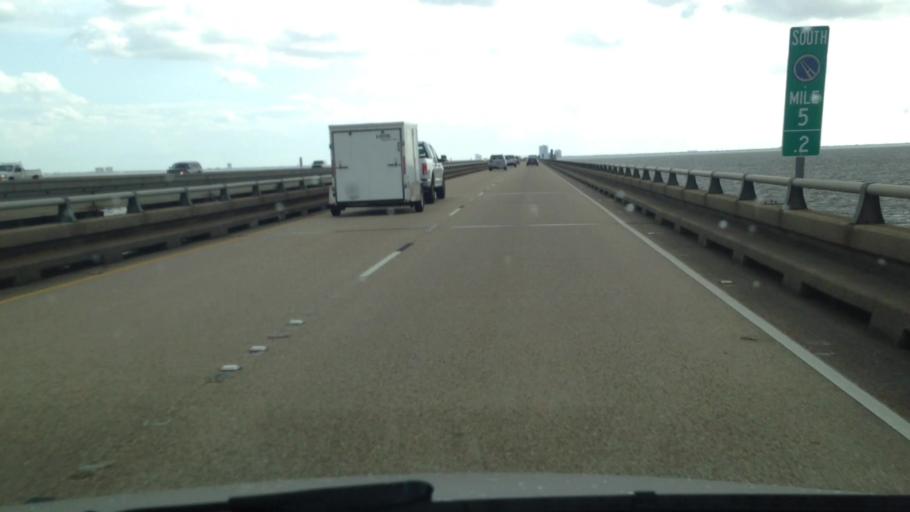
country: US
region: Louisiana
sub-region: Jefferson Parish
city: Metairie
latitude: 30.0965
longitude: -90.1411
